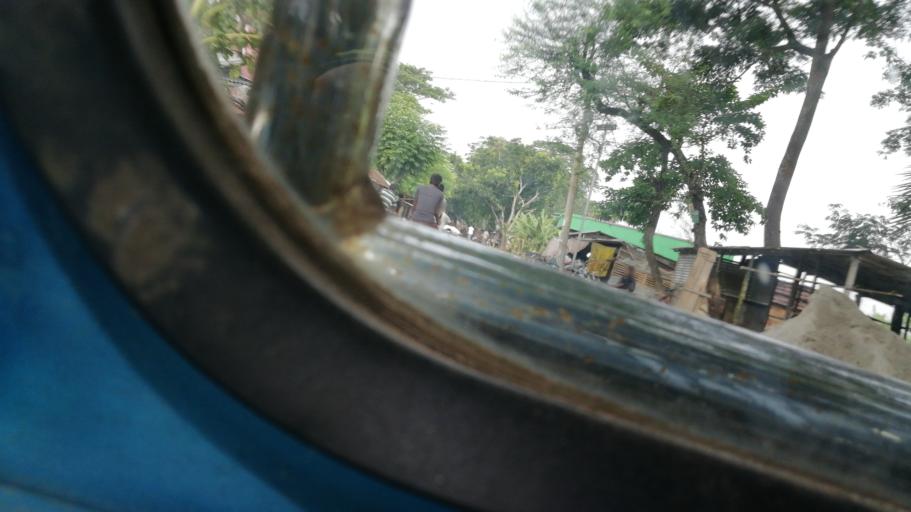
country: BD
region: Khulna
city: Kesabpur
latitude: 23.0315
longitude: 89.2752
